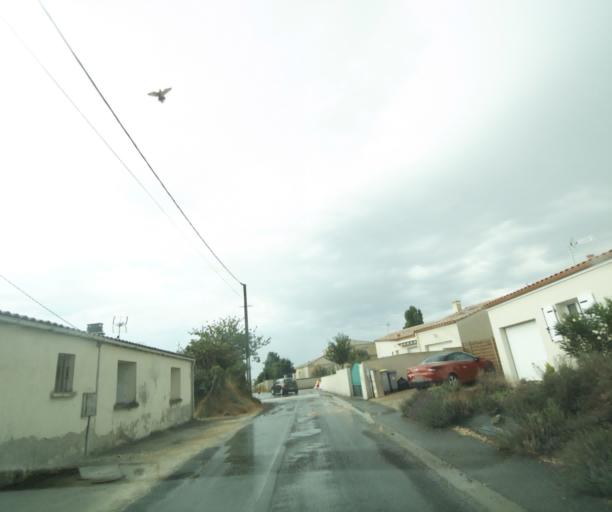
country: FR
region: Poitou-Charentes
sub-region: Departement de la Charente-Maritime
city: Tonnay-Charente
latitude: 45.9500
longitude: -0.8816
